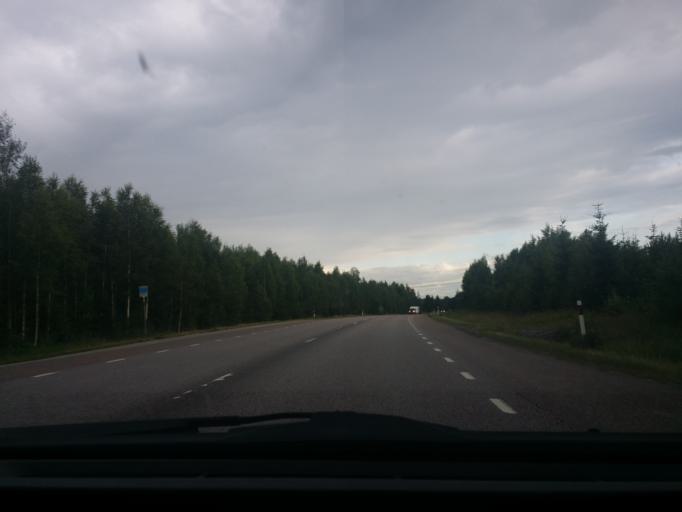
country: SE
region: OErebro
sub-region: Orebro Kommun
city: Hovsta
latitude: 59.4346
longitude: 15.1620
